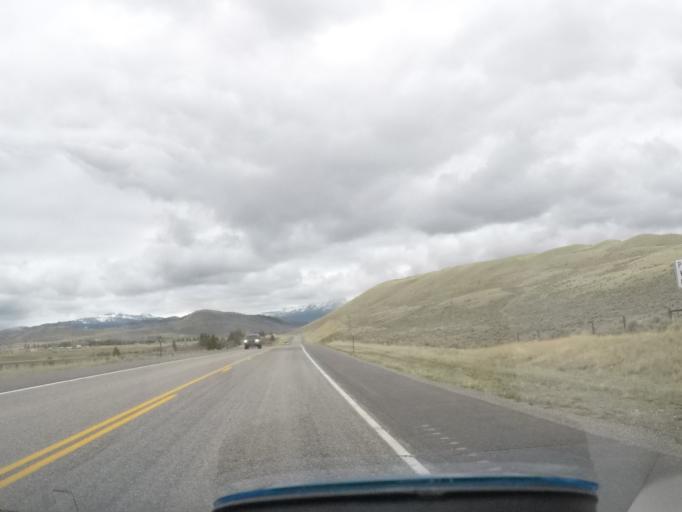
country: US
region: Wyoming
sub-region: Sublette County
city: Pinedale
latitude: 43.5882
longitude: -109.7719
